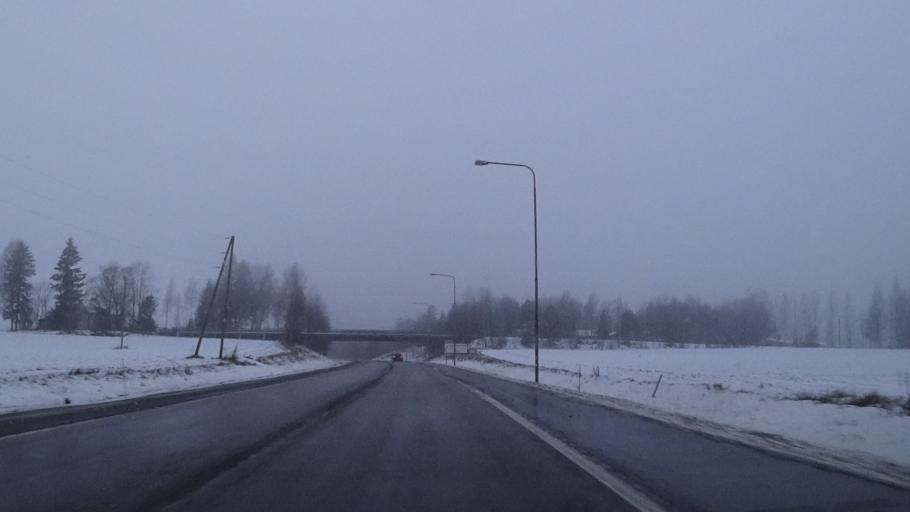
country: FI
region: Paijanne Tavastia
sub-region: Lahti
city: Hollola
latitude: 60.9835
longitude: 25.4527
